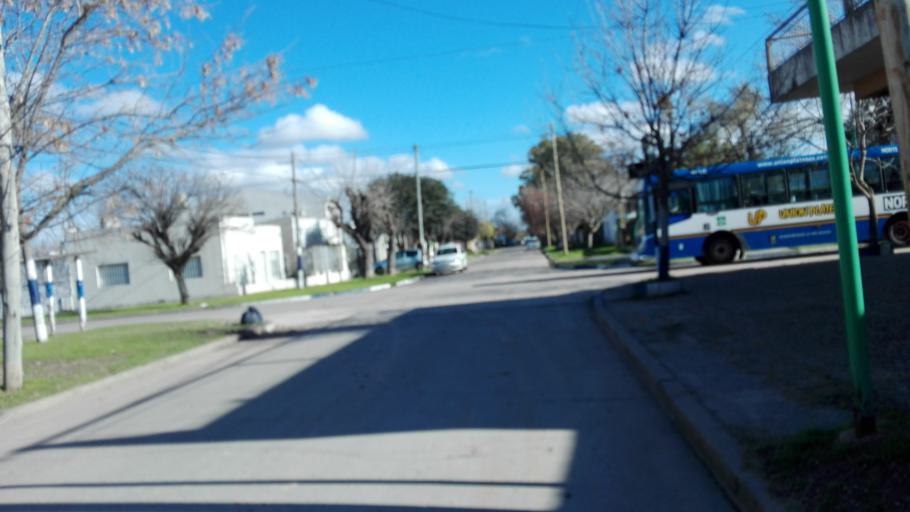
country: AR
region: Buenos Aires
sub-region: Partido de La Plata
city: La Plata
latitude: -34.8807
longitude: -57.9883
